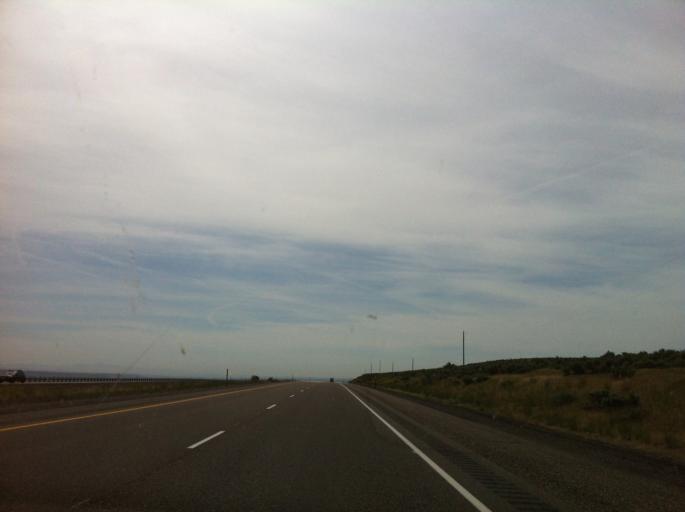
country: US
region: Oregon
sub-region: Malheur County
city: Ontario
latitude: 44.1162
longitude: -117.0627
